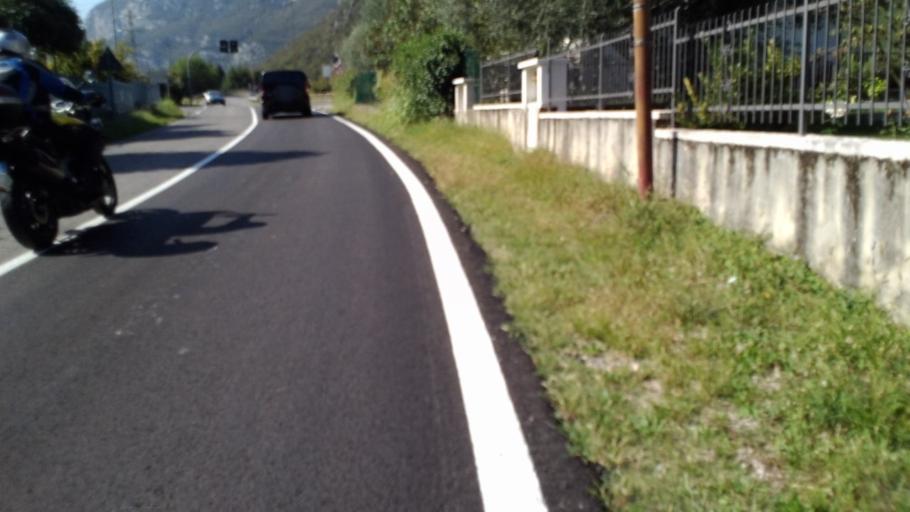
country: IT
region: Veneto
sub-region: Provincia di Verona
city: Brentino Belluno
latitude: 45.6543
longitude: 10.8923
